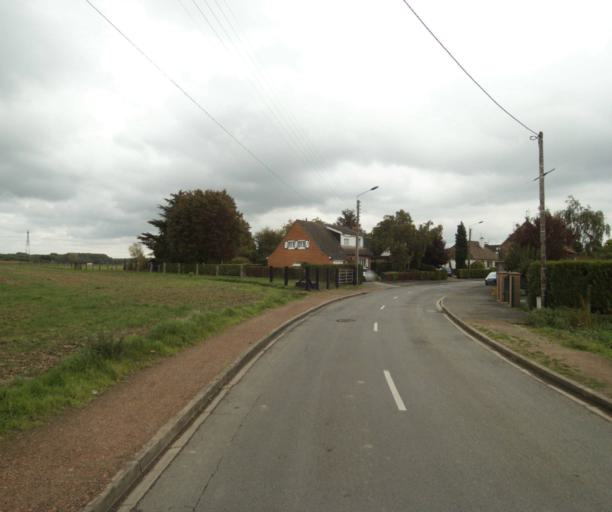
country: FR
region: Nord-Pas-de-Calais
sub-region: Departement du Nord
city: Wavrin
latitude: 50.5751
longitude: 2.9479
